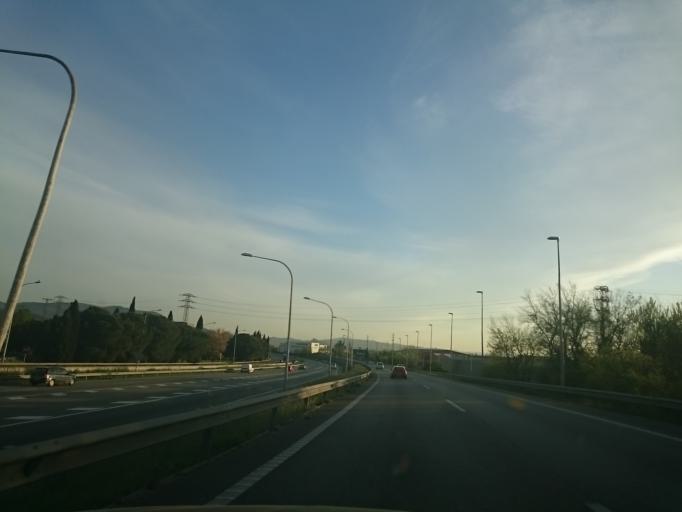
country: ES
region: Catalonia
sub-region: Provincia de Barcelona
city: Montmelo
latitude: 41.5551
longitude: 2.2390
